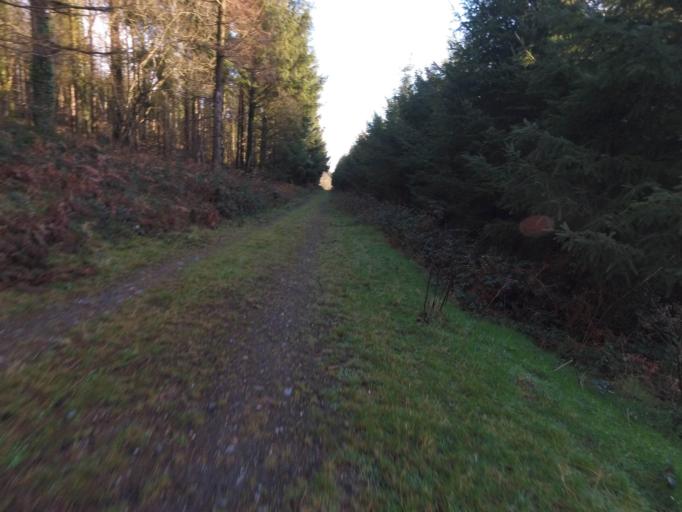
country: IE
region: Munster
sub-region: Waterford
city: Portlaw
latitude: 52.3060
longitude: -7.3538
